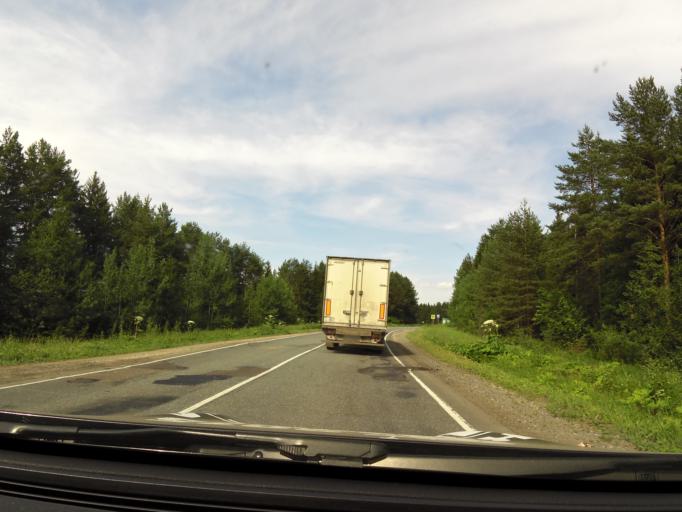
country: RU
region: Kirov
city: Slobodskoy
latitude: 58.7562
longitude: 50.3258
